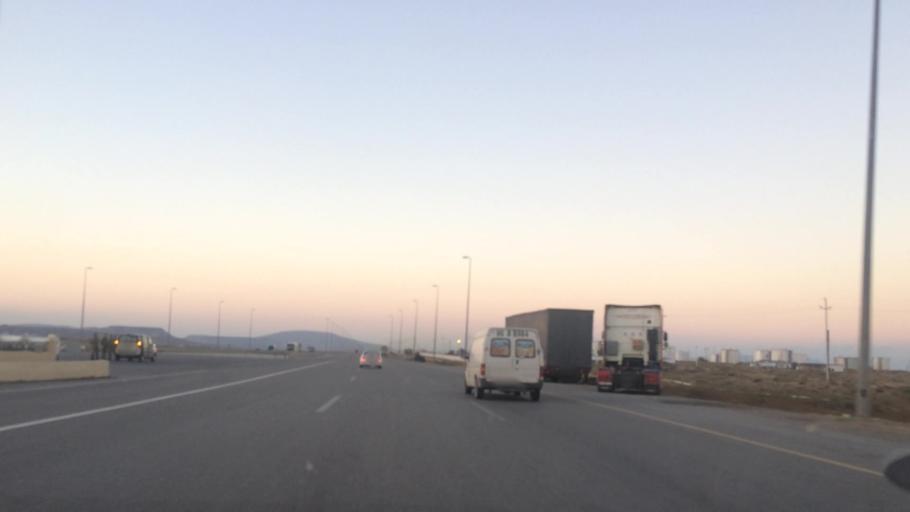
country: AZ
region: Baki
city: Qobustan
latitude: 39.9950
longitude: 49.4310
